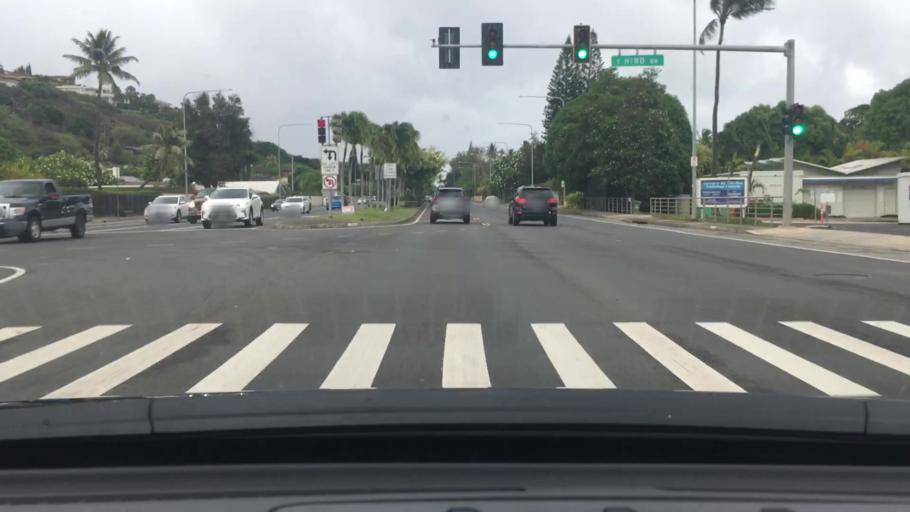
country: US
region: Hawaii
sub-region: Honolulu County
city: Waimanalo
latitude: 21.2786
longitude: -157.7497
